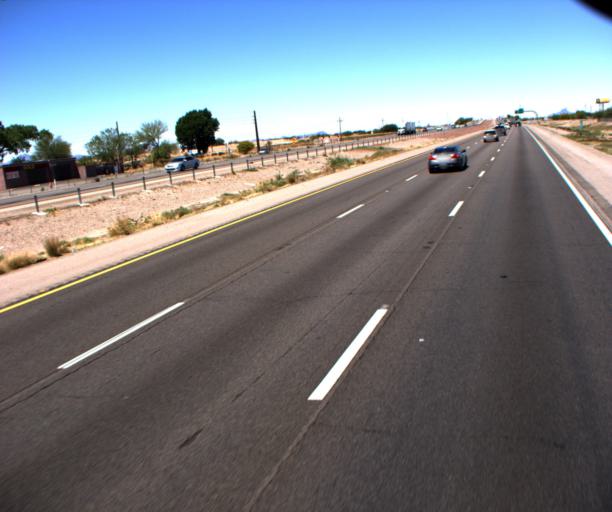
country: US
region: Arizona
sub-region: Pima County
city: Marana
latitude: 32.4189
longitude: -111.1558
